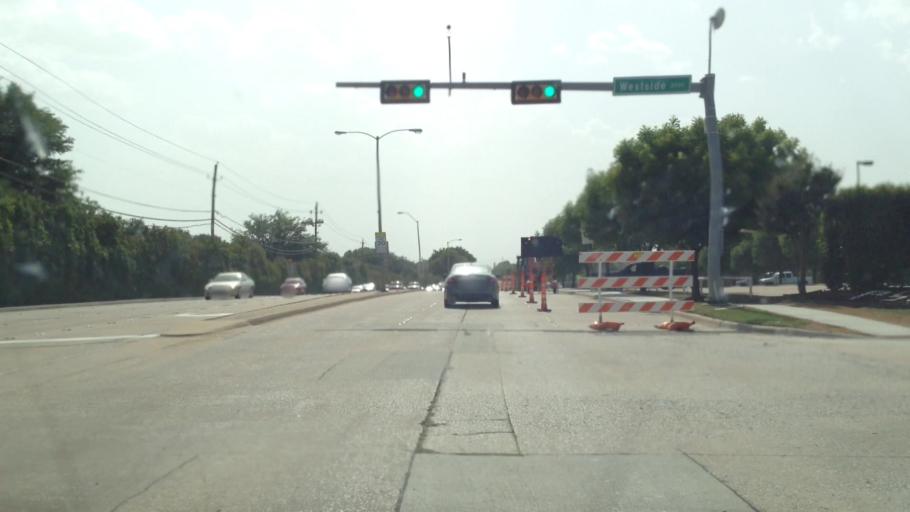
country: US
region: Texas
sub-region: Collin County
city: Plano
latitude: 33.0267
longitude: -96.7480
